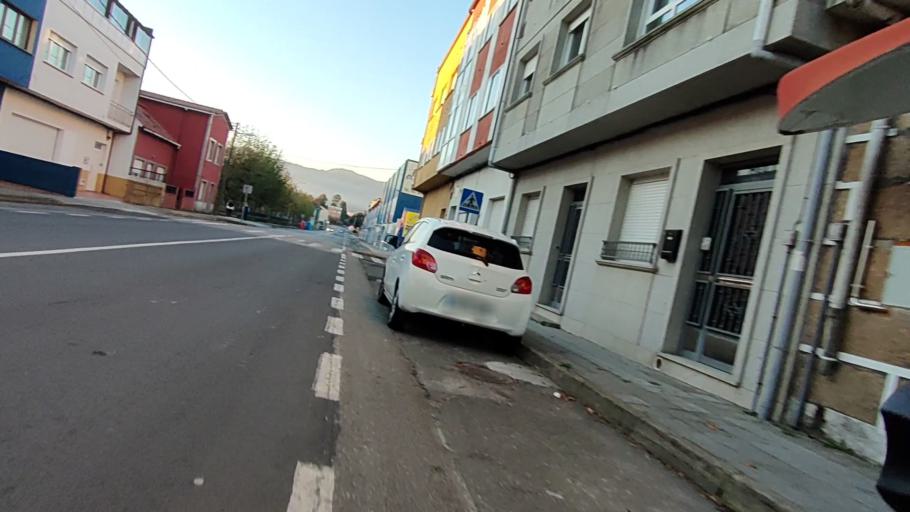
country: ES
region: Galicia
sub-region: Provincia da Coruna
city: Boiro
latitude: 42.6382
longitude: -8.8783
